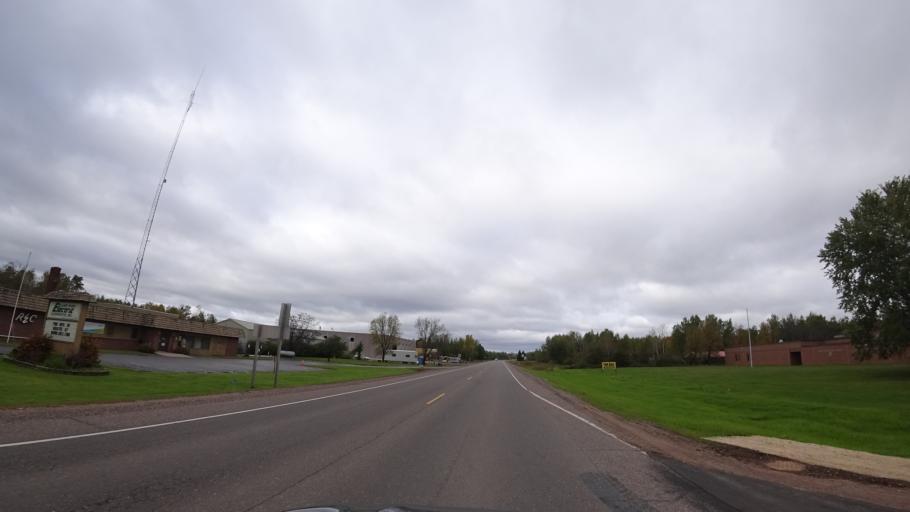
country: US
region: Wisconsin
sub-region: Rusk County
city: Ladysmith
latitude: 45.4758
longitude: -91.1110
